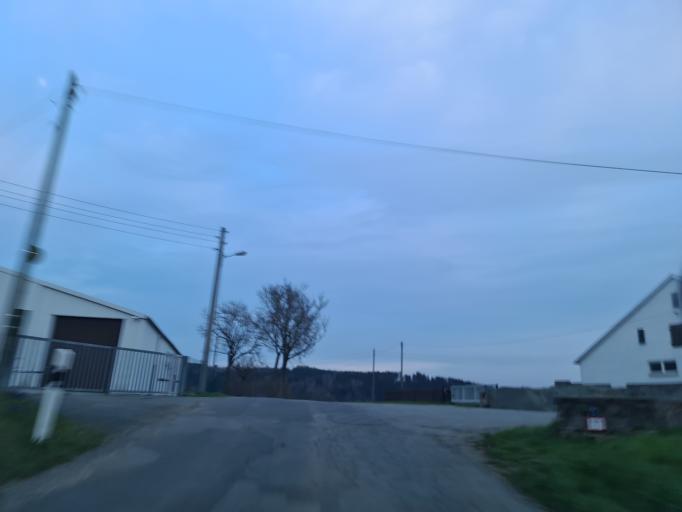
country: DE
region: Saxony
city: Bosenbrunn
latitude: 50.4200
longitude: 12.0976
